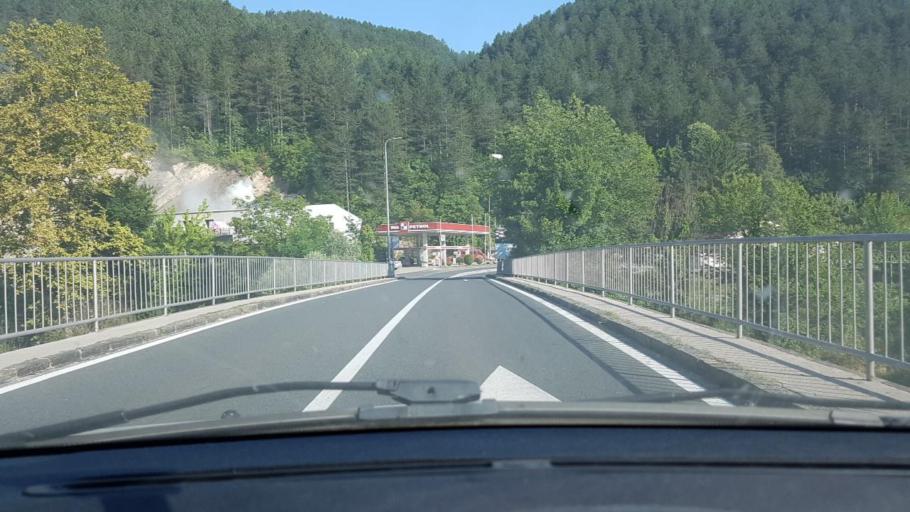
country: BA
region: Federation of Bosnia and Herzegovina
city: Ostrozac
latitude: 44.8971
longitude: 15.9349
